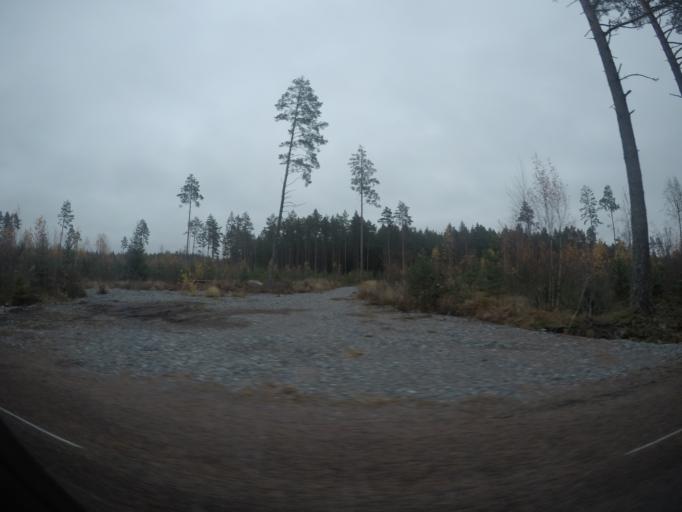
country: SE
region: Vaestmanland
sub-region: Surahammars Kommun
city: Surahammar
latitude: 59.6654
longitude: 16.0824
